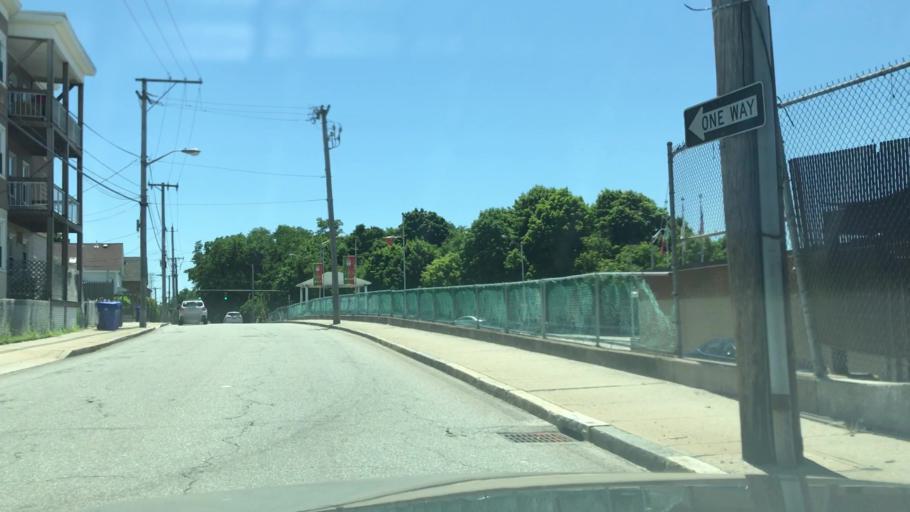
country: US
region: Rhode Island
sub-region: Providence County
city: Pawtucket
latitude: 41.8725
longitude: -71.3807
